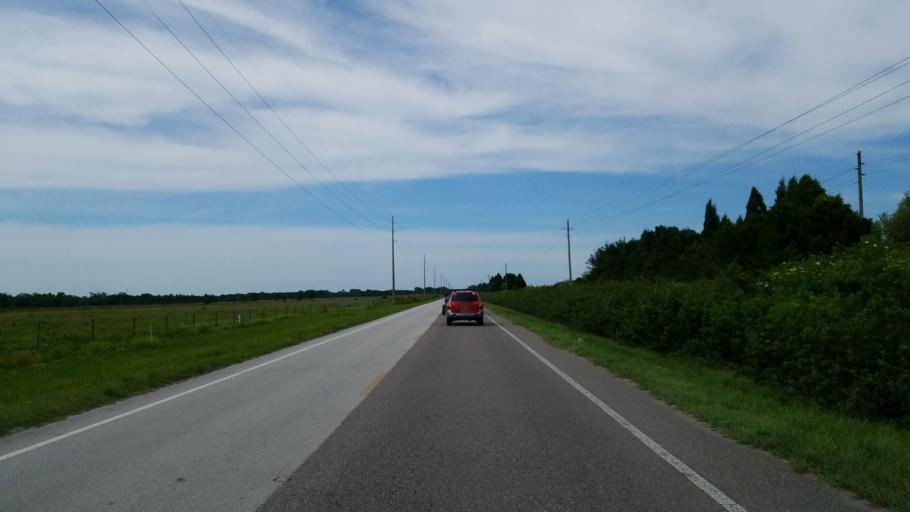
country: US
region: Florida
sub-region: Hillsborough County
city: Balm
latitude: 27.6609
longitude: -82.1462
